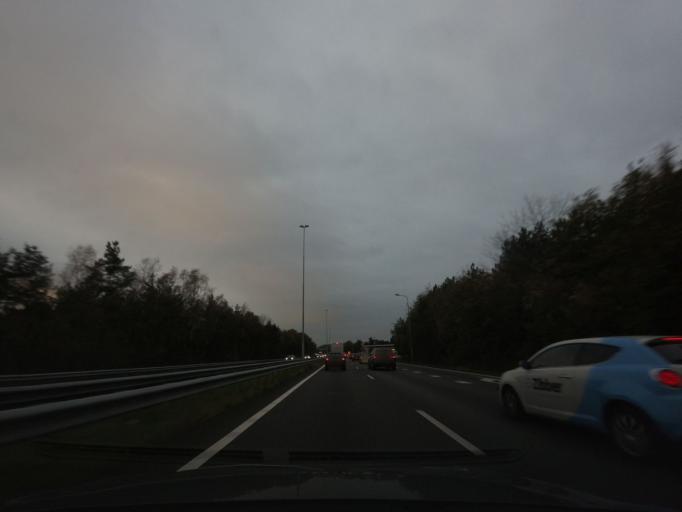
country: NL
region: North Brabant
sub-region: Gemeente Oosterhout
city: Oosterhout
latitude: 51.6042
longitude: 4.8445
